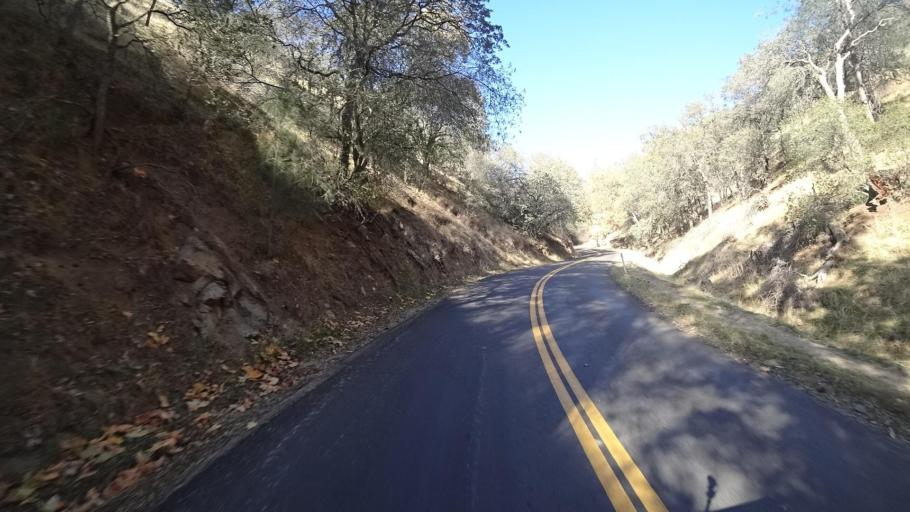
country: US
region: California
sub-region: Kern County
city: Bear Valley Springs
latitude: 35.3257
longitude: -118.5910
